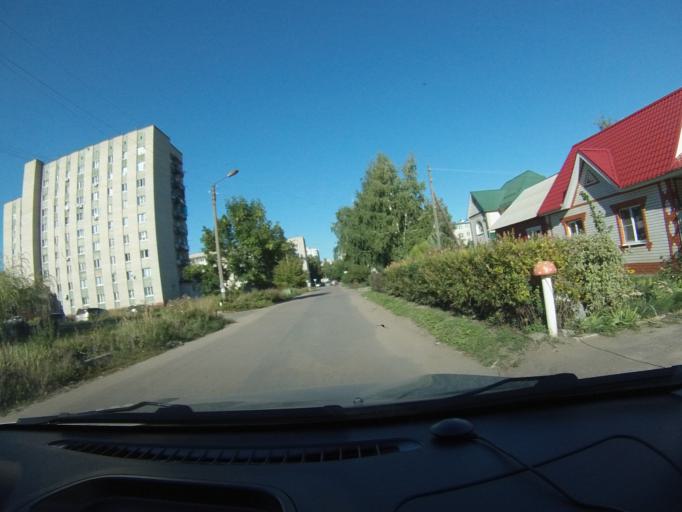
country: RU
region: Tambov
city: Tambov
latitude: 52.7644
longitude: 41.4126
